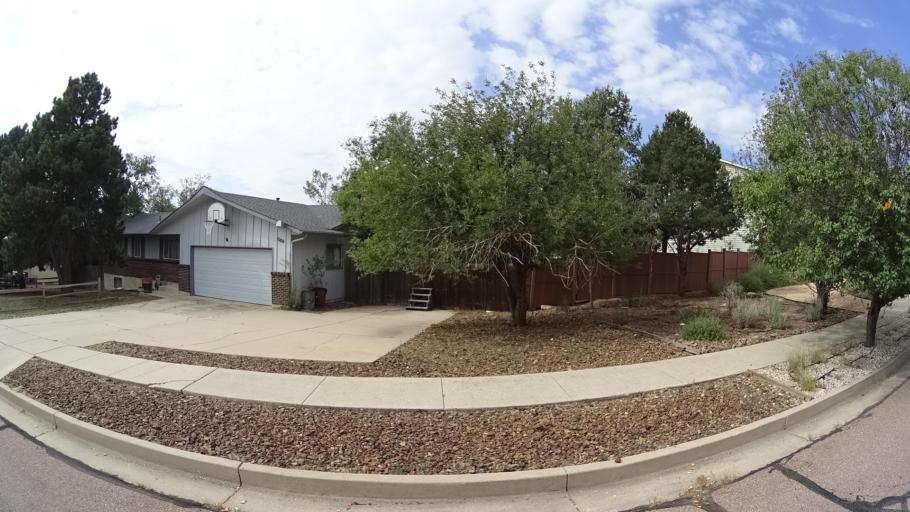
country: US
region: Colorado
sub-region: El Paso County
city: Cimarron Hills
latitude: 38.8498
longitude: -104.7248
